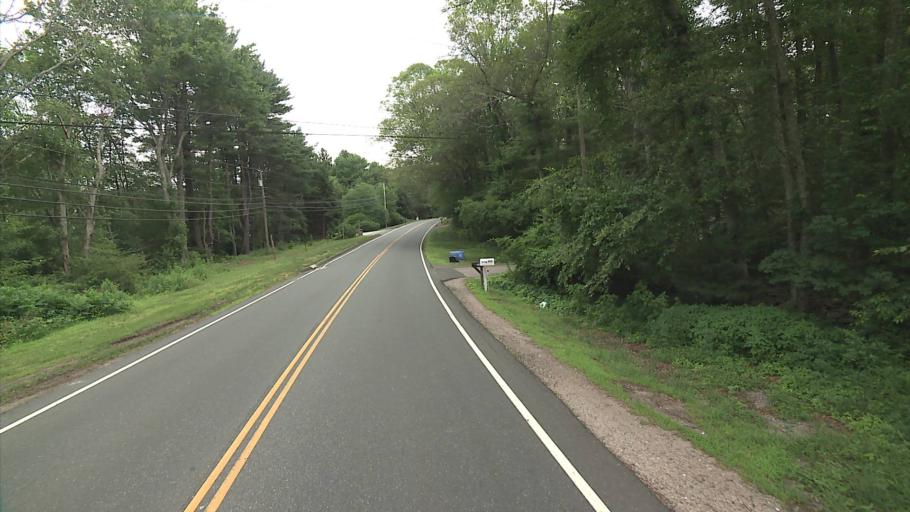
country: US
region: Connecticut
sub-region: New London County
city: Ledyard Center
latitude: 41.4530
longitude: -72.0171
